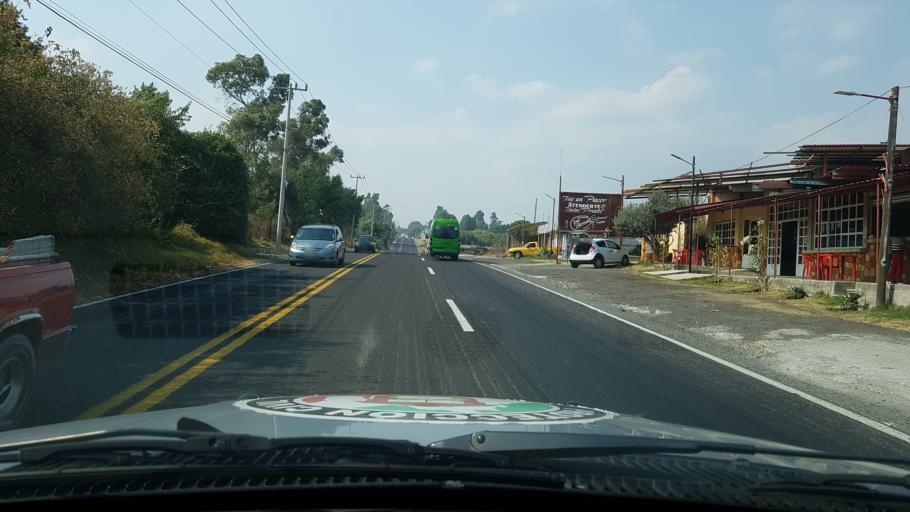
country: MX
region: Mexico
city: Tepetlixpa
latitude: 19.0129
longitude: -98.8242
